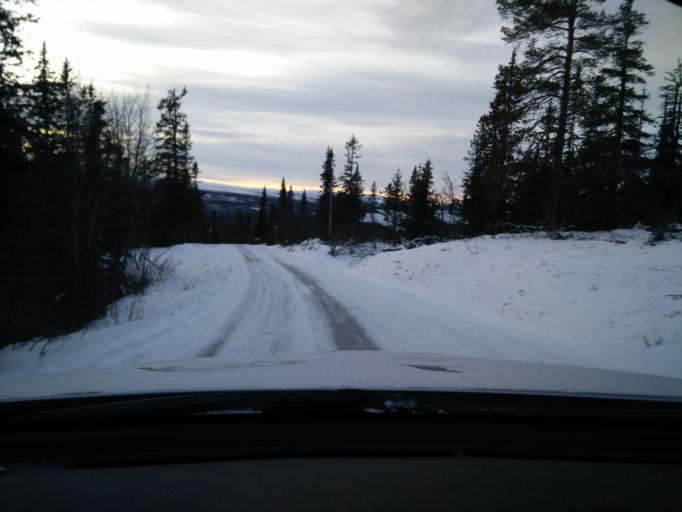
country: SE
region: Jaemtland
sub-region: Bergs Kommun
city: Hoverberg
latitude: 62.4904
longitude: 14.1470
